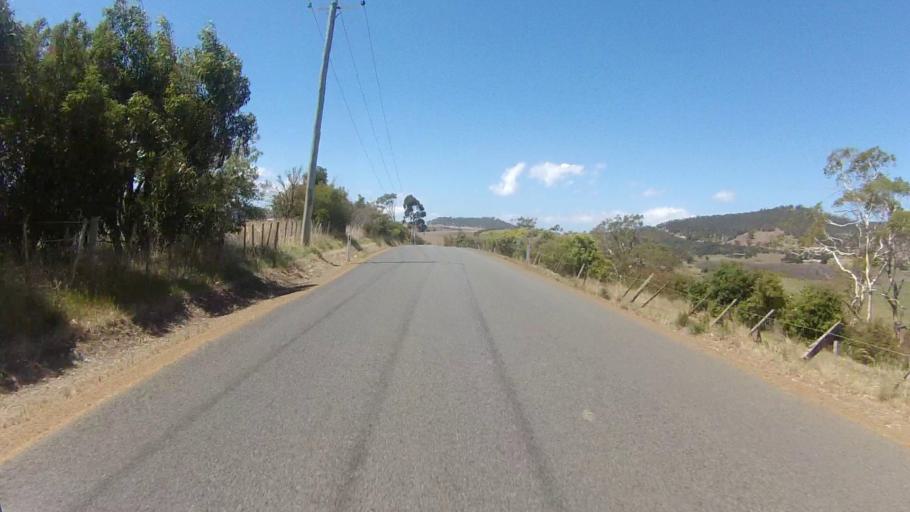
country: AU
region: Tasmania
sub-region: Sorell
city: Sorell
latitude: -42.7724
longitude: 147.5900
